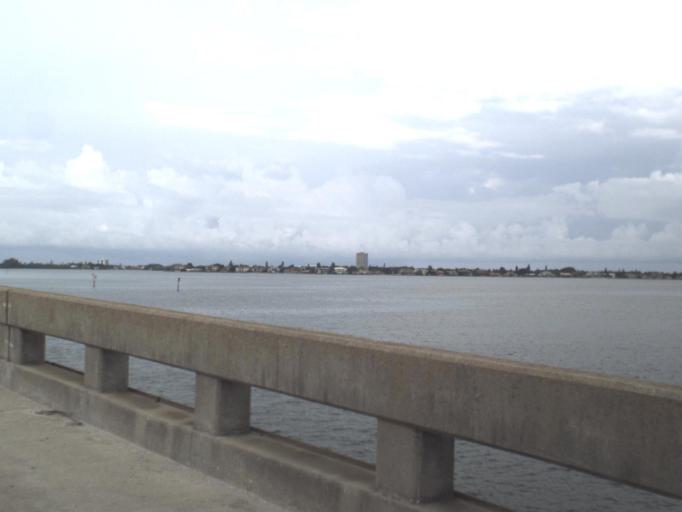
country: US
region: Florida
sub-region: Sarasota County
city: Siesta Key
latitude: 27.3028
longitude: -82.5429
